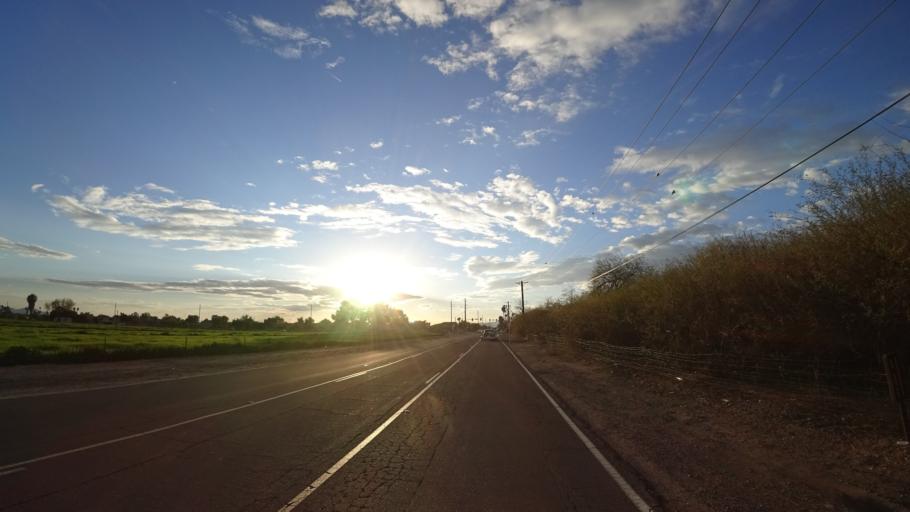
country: US
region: Arizona
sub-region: Maricopa County
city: Glendale
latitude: 33.5452
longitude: -112.2184
